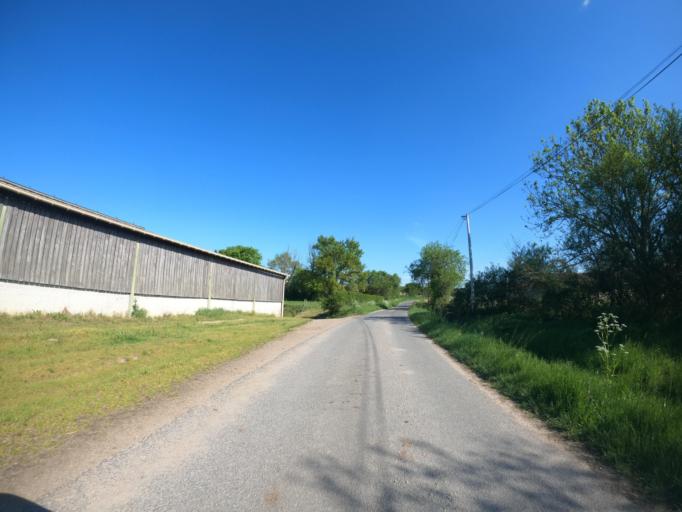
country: FR
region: Poitou-Charentes
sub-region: Departement des Deux-Sevres
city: Moncoutant
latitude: 46.6846
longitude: -0.5413
